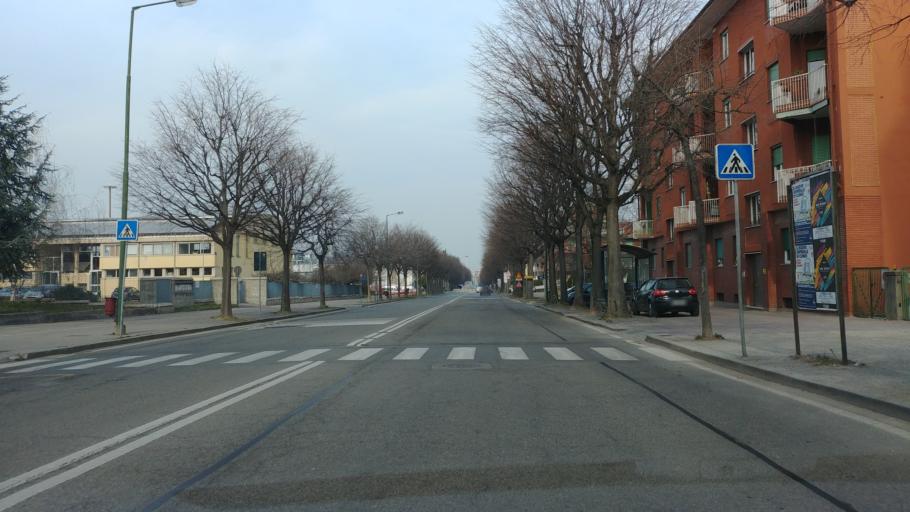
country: IT
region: Piedmont
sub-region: Provincia di Cuneo
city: Cuneo
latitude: 44.3780
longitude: 7.5279
